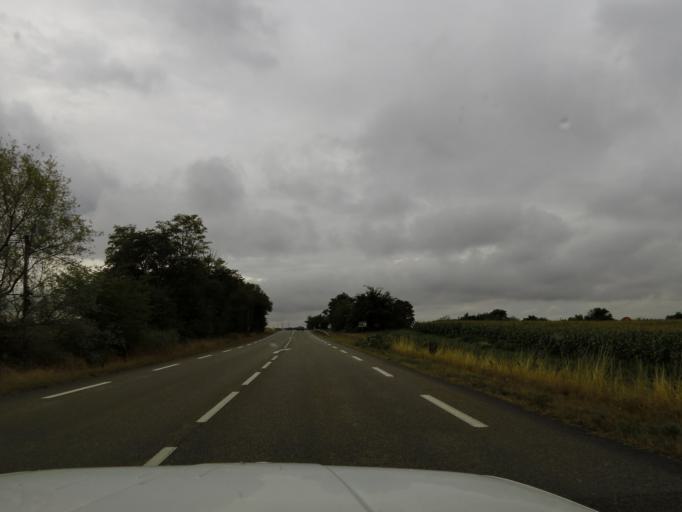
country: FR
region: Rhone-Alpes
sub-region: Departement de l'Ain
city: Perouges
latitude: 45.8787
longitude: 5.1838
